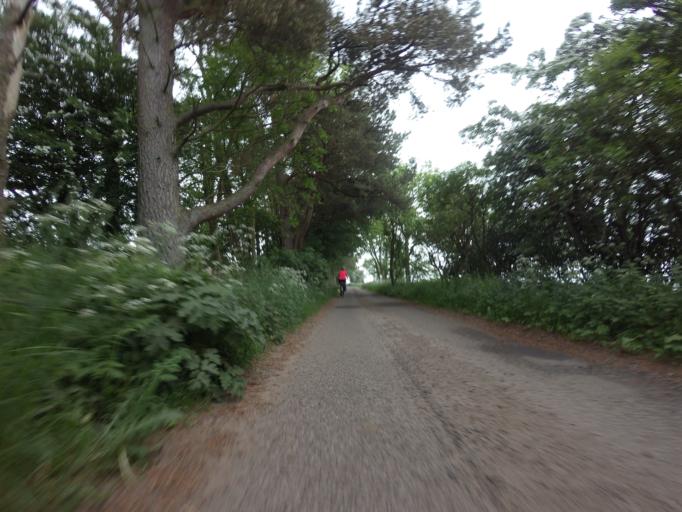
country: GB
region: Scotland
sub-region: Fife
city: Ballingry
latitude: 56.2316
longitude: -3.3431
